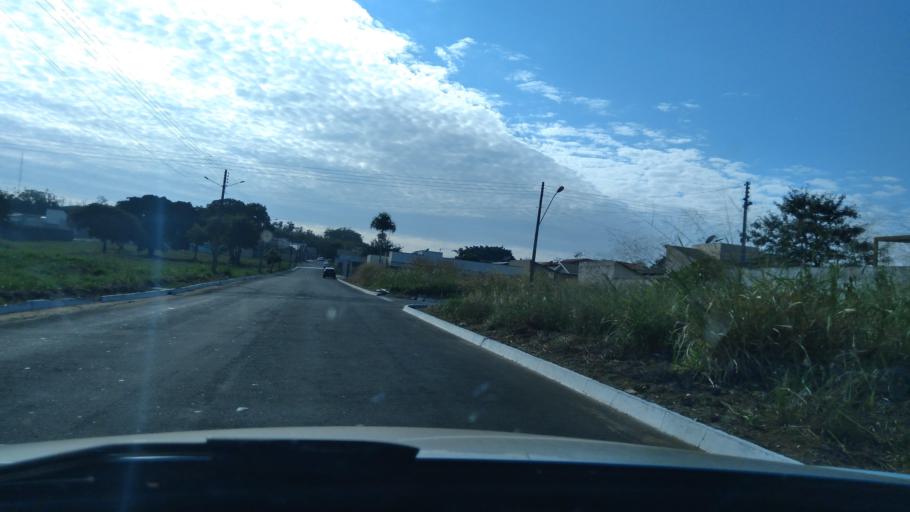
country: BR
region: Goias
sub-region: Mineiros
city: Mineiros
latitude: -17.5553
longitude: -52.5613
